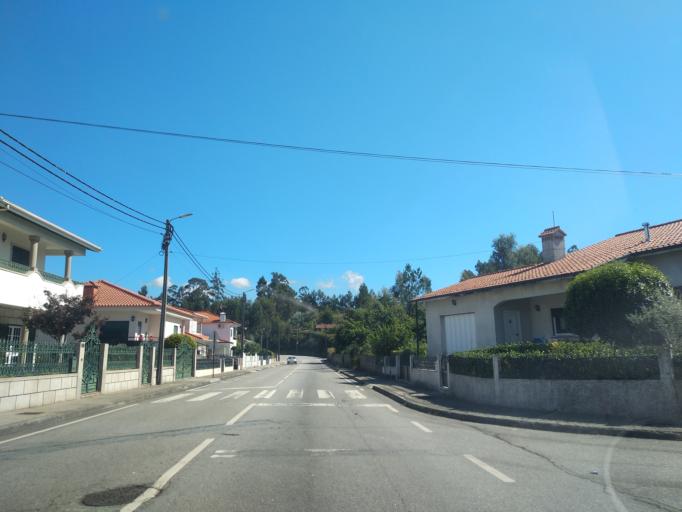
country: PT
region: Porto
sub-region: Pacos de Ferreira
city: Ferreira
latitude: 41.2651
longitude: -8.3341
